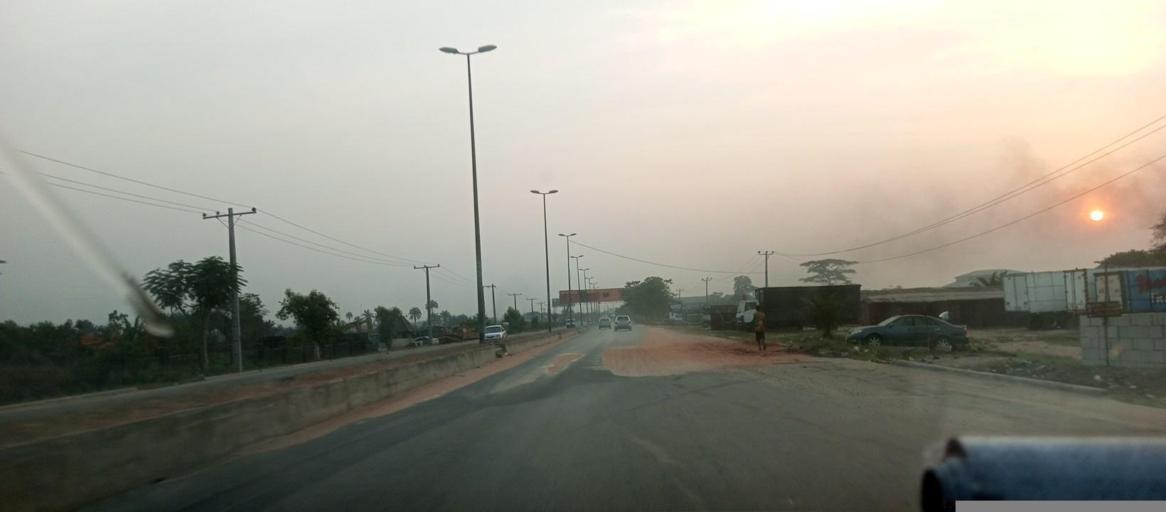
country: NG
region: Rivers
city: Emuoha
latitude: 4.9309
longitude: 7.0021
